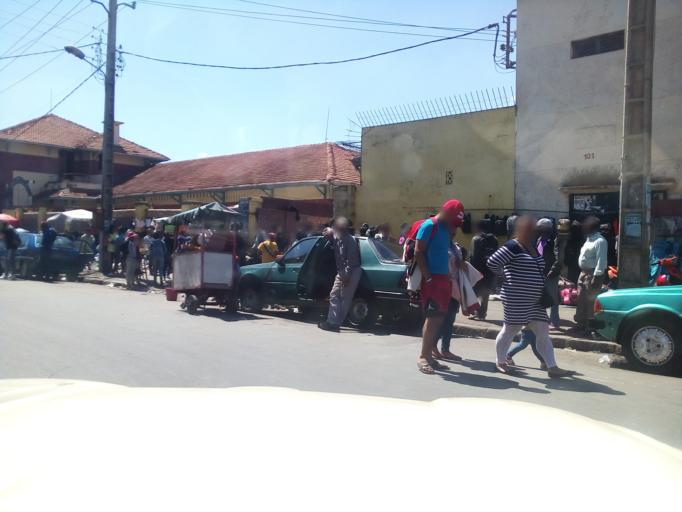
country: MG
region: Analamanga
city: Antananarivo
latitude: -18.9058
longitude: 47.5248
